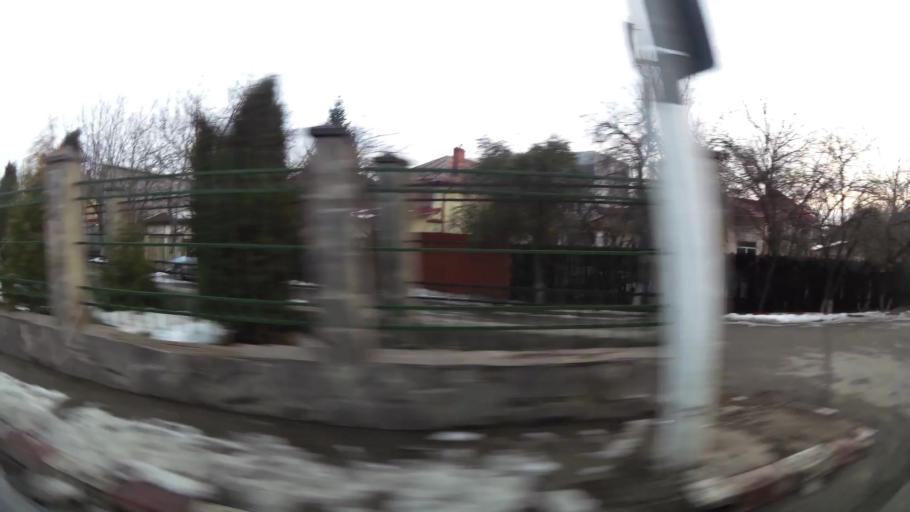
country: RO
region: Ilfov
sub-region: Comuna Fundeni-Dobroesti
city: Fundeni
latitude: 44.4554
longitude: 26.1698
